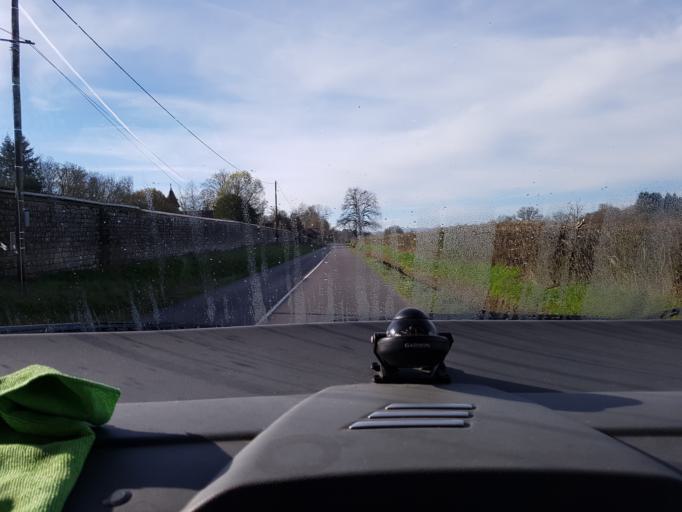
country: FR
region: Bourgogne
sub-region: Departement de Saone-et-Loire
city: Etang-sur-Arroux
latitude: 46.8592
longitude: 4.1945
